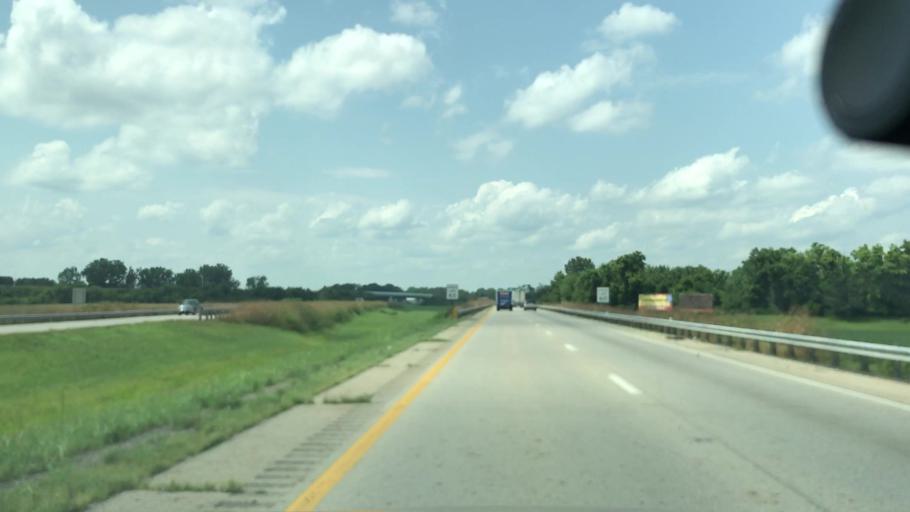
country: US
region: Ohio
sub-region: Ross County
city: Chillicothe
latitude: 39.3175
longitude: -82.9335
